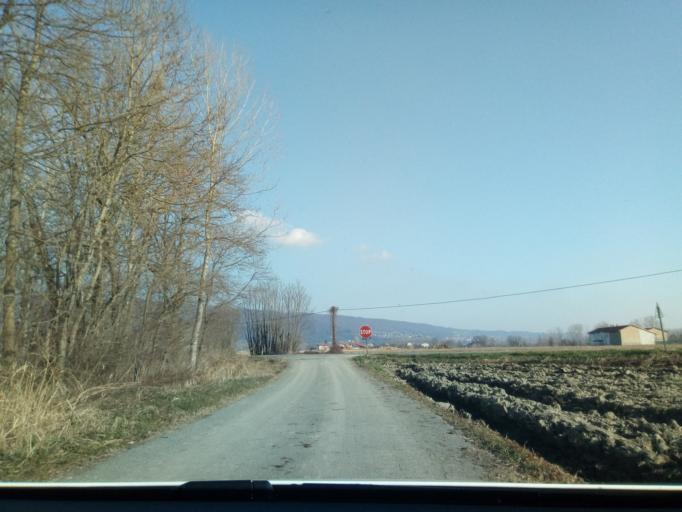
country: IT
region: Piedmont
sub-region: Provincia di Torino
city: Albiano d'Ivrea
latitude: 45.4511
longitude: 7.9406
